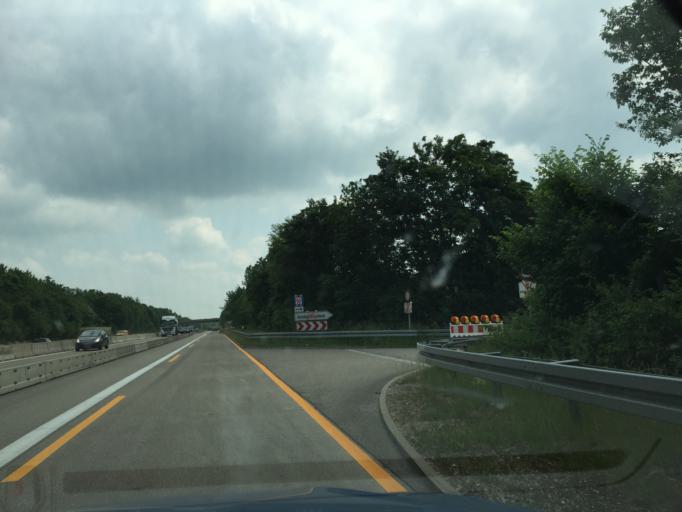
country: DE
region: Baden-Wuerttemberg
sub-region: Regierungsbezirk Stuttgart
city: Nattheim
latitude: 48.6702
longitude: 10.2252
